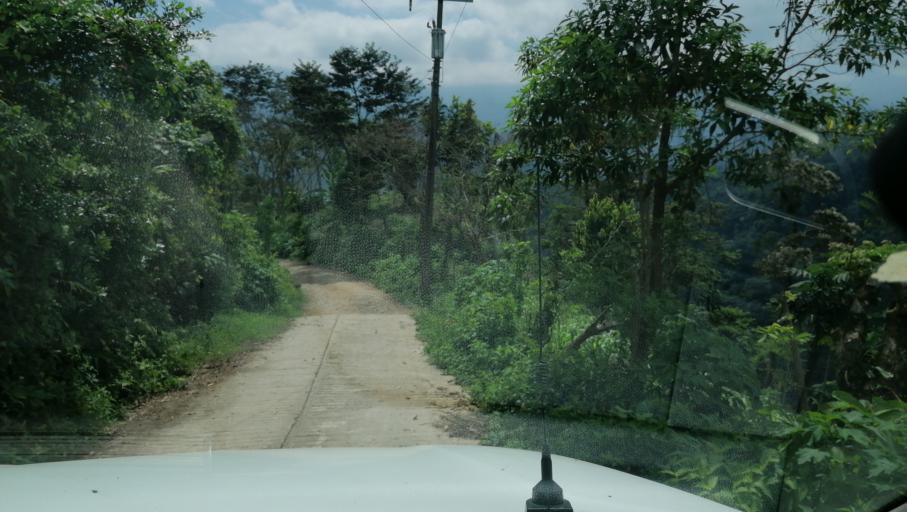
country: MX
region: Chiapas
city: Ixtacomitan
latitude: 17.3575
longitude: -93.1204
